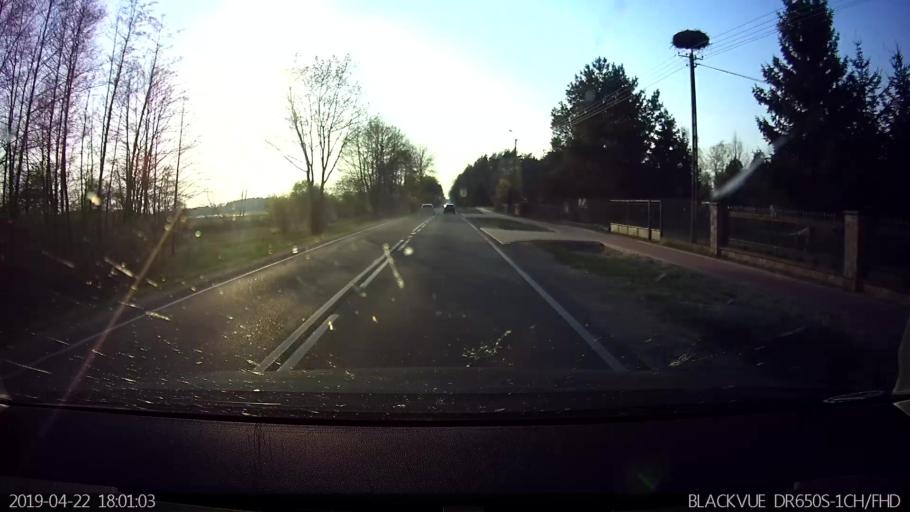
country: PL
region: Masovian Voivodeship
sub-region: Powiat wegrowski
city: Korytnica
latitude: 52.4772
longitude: 21.8366
